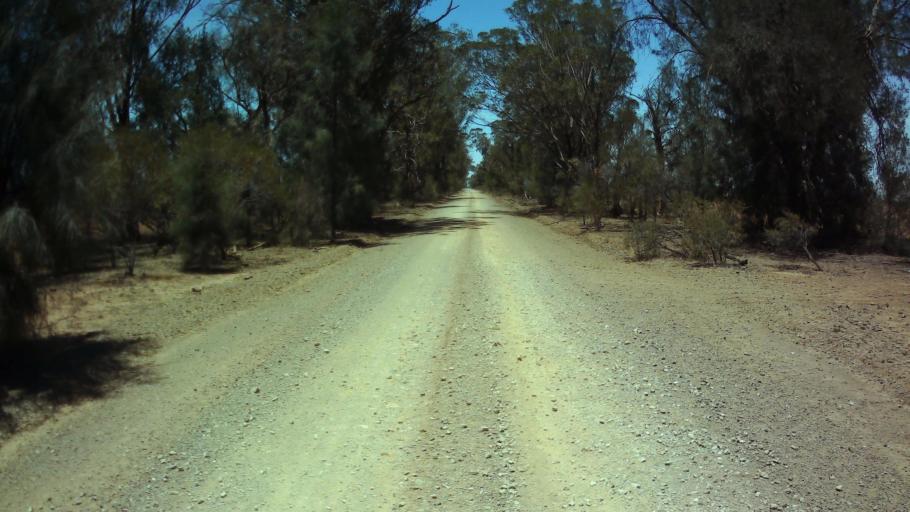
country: AU
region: New South Wales
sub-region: Weddin
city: Grenfell
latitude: -33.9378
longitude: 147.7124
